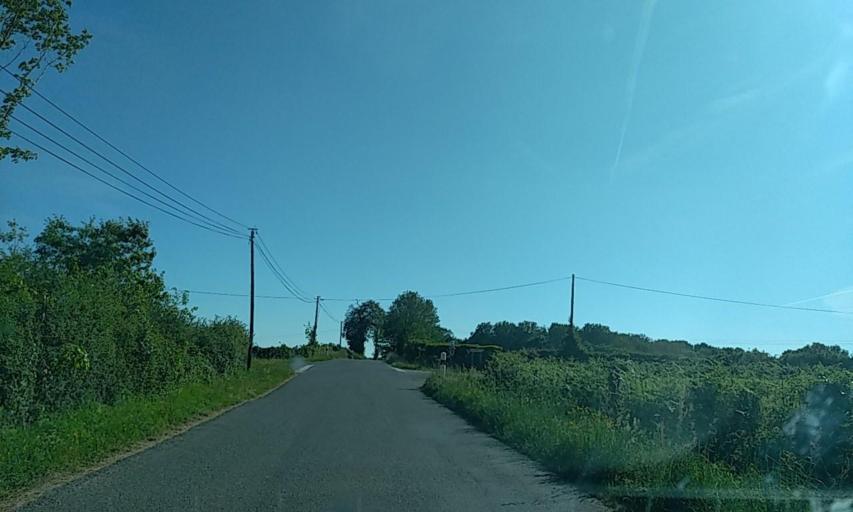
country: FR
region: Poitou-Charentes
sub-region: Departement des Deux-Sevres
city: Boisme
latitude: 46.7928
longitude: -0.4285
